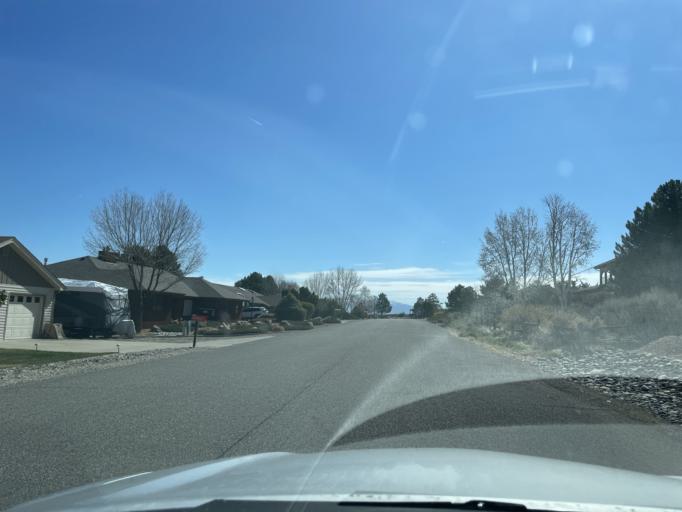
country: US
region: Colorado
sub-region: Mesa County
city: Redlands
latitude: 39.0760
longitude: -108.6730
